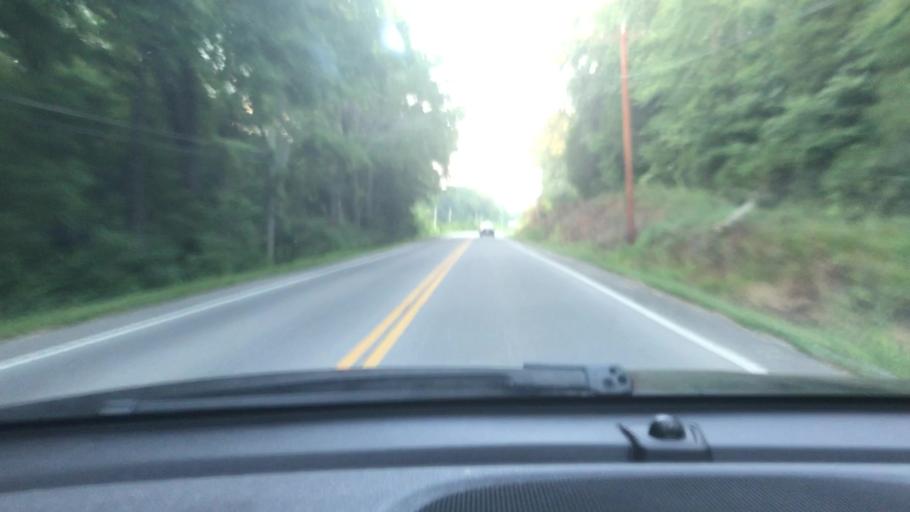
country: US
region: Tennessee
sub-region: Dickson County
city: Dickson
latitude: 36.1166
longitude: -87.3666
